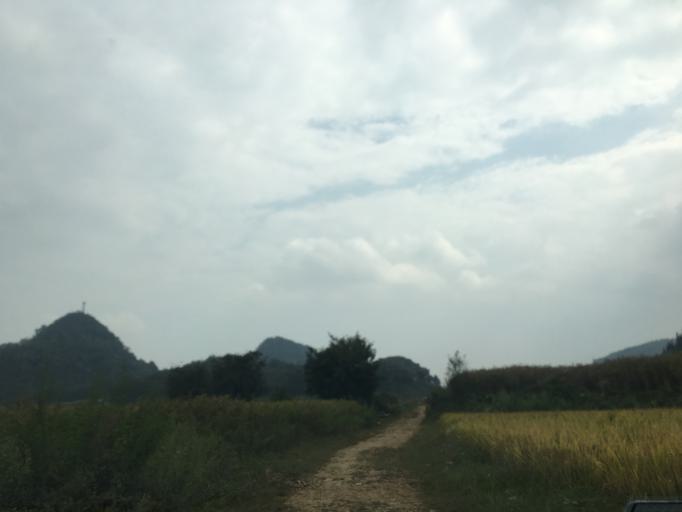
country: CN
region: Guangxi Zhuangzu Zizhiqu
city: Xinzhou
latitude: 25.4927
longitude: 105.6521
